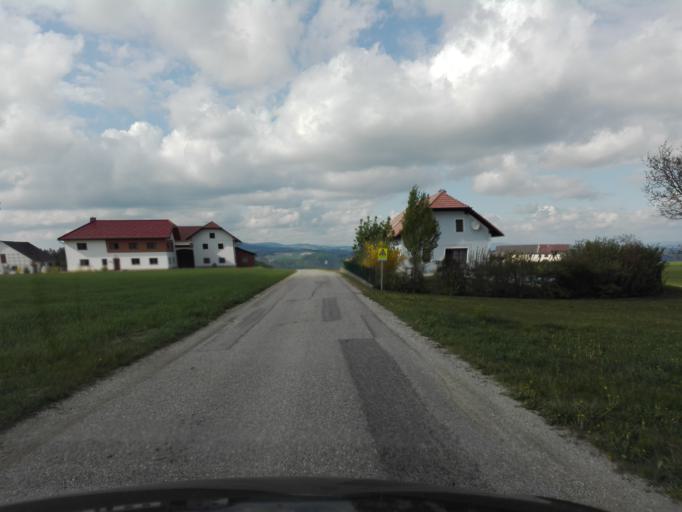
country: AT
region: Upper Austria
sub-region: Politischer Bezirk Rohrbach
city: Pfarrkirchen im Muehlkreis
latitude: 48.4087
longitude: 13.8594
